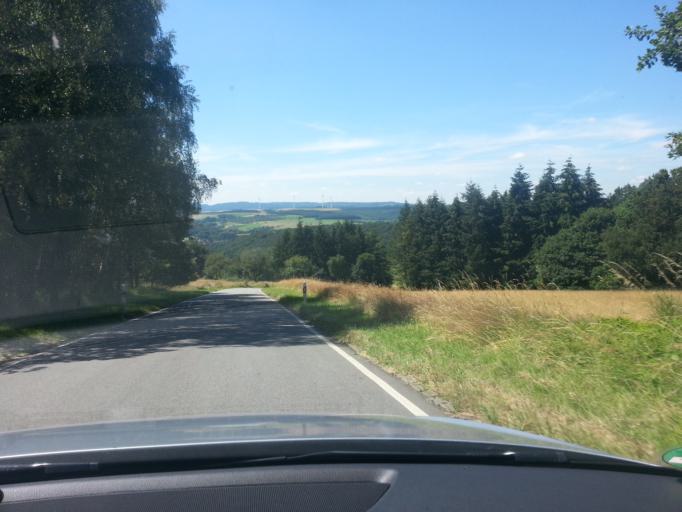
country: DE
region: Rheinland-Pfalz
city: Fockelberg
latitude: 49.5408
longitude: 7.4846
